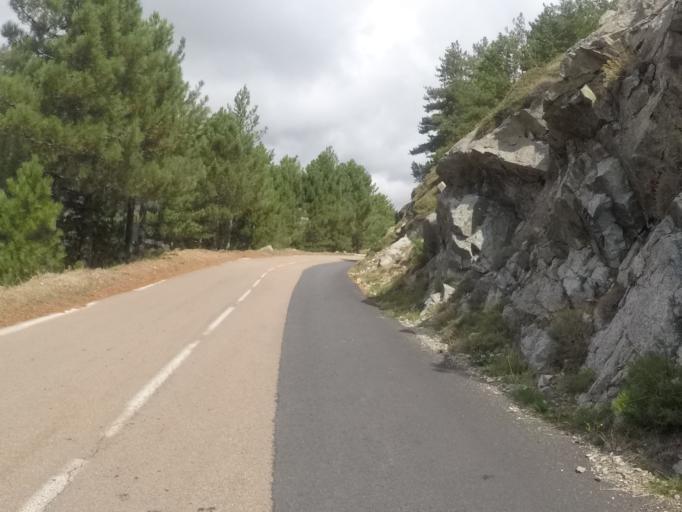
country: FR
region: Corsica
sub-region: Departement de la Corse-du-Sud
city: Zonza
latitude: 41.7857
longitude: 9.2197
